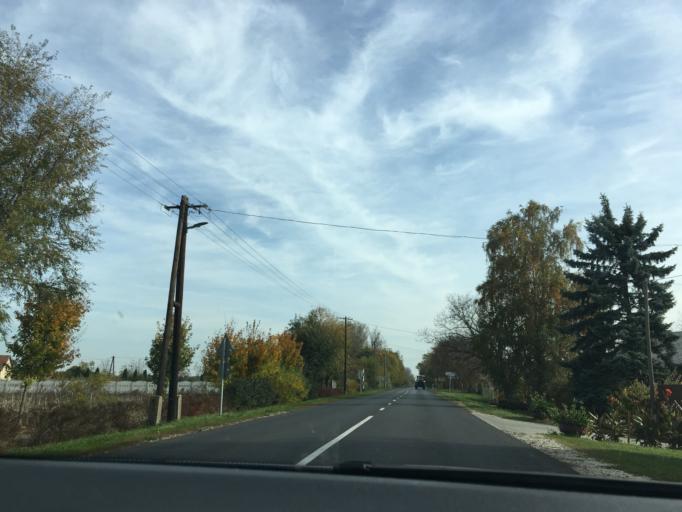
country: HU
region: Szabolcs-Szatmar-Bereg
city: Nagykallo
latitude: 47.8700
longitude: 21.8711
